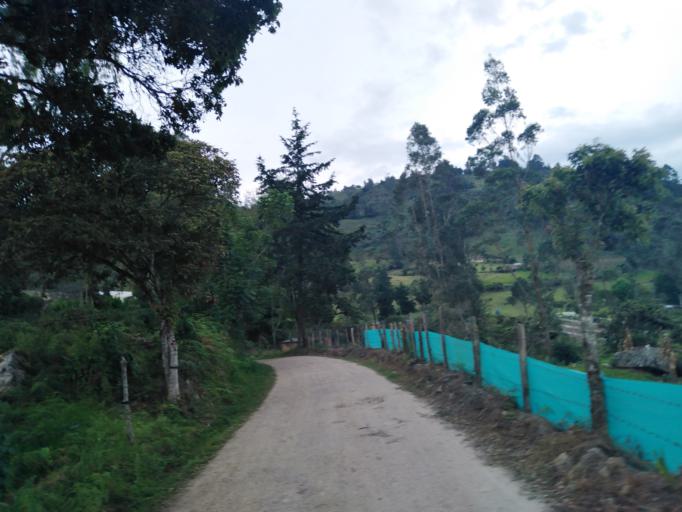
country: CO
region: Cundinamarca
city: Tenza
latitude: 5.1185
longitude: -73.4074
